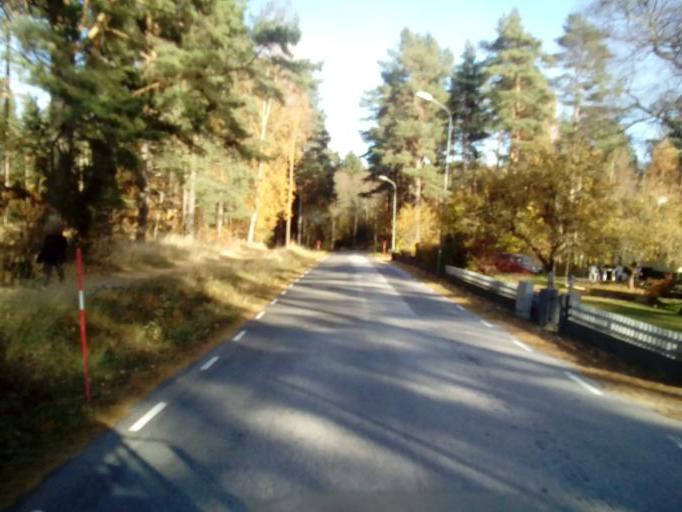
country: SE
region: Kalmar
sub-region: Vimmerby Kommun
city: Vimmerby
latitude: 57.6733
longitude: 15.8728
